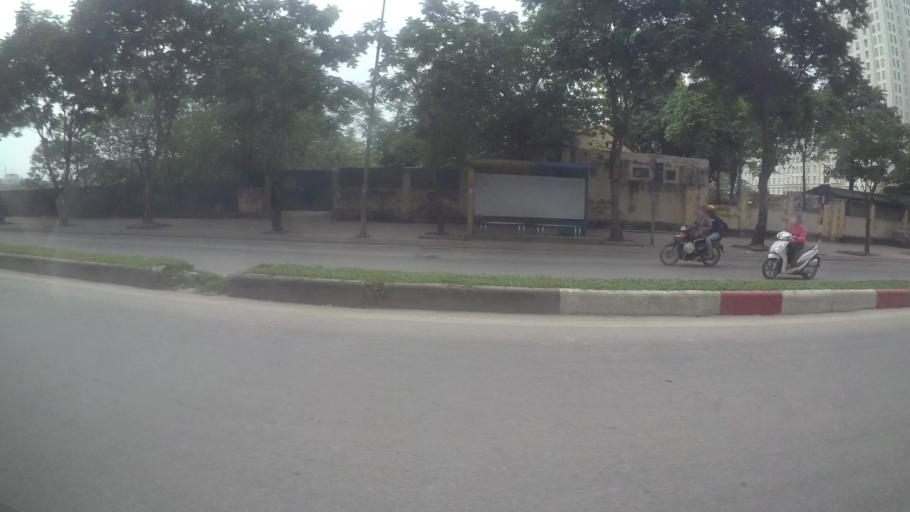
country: VN
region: Ha Noi
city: Cau Dien
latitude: 21.0123
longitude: 105.7745
